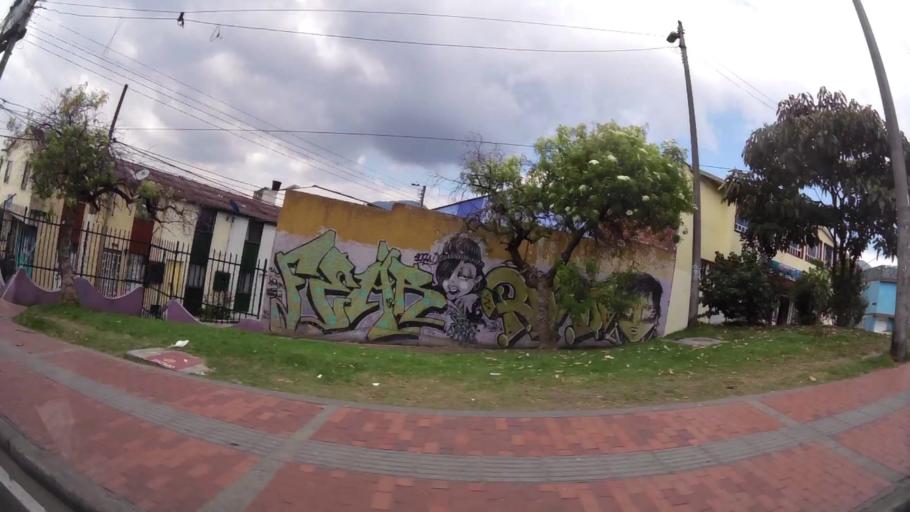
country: CO
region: Bogota D.C.
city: Bogota
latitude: 4.5598
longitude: -74.0990
